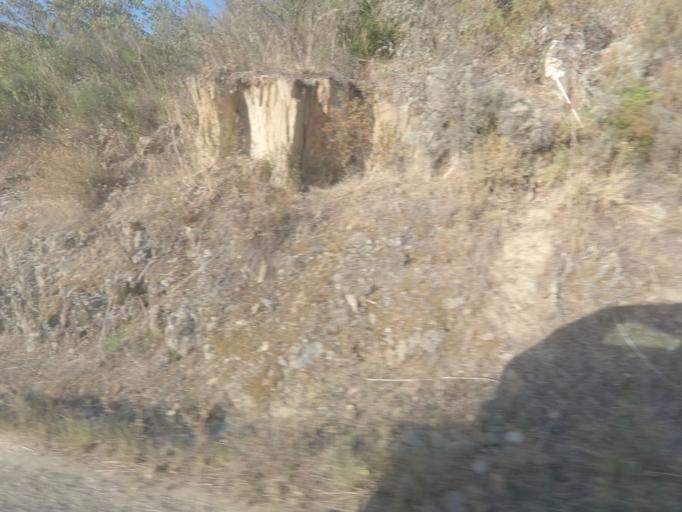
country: PT
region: Viseu
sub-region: Armamar
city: Armamar
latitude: 41.1298
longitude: -7.6739
